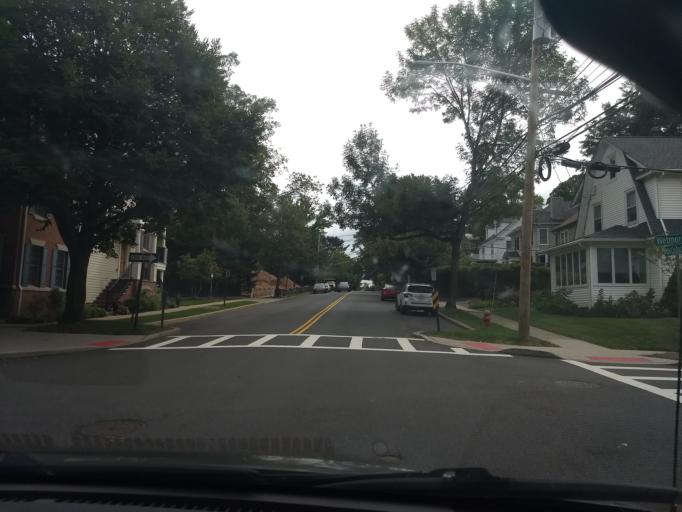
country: US
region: New Jersey
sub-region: Morris County
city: Morristown
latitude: 40.7936
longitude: -74.4831
